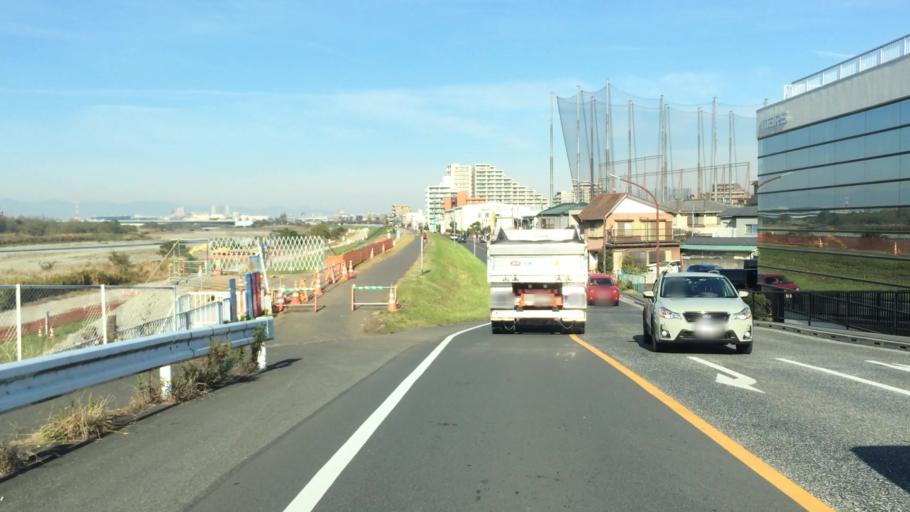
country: JP
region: Tokyo
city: Chofugaoka
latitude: 35.6451
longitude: 139.5265
